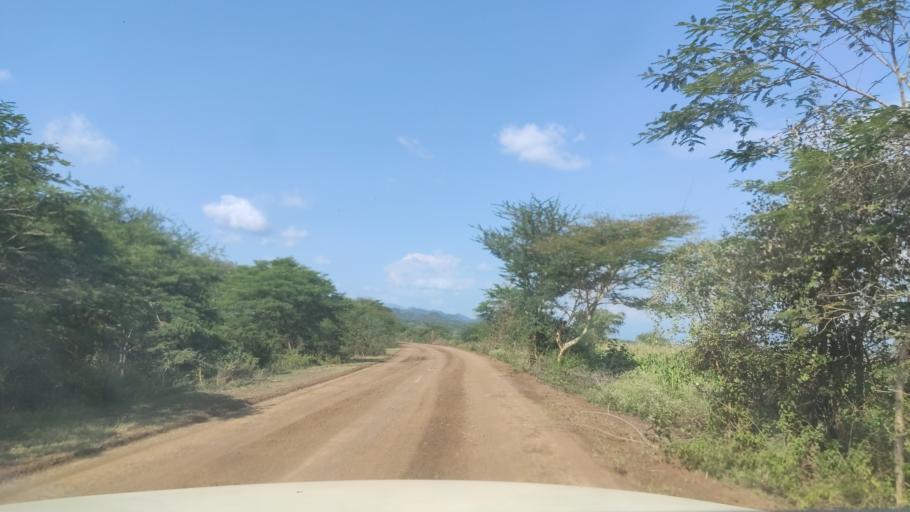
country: ET
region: Southern Nations, Nationalities, and People's Region
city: Felege Neway
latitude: 6.3829
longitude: 37.0940
